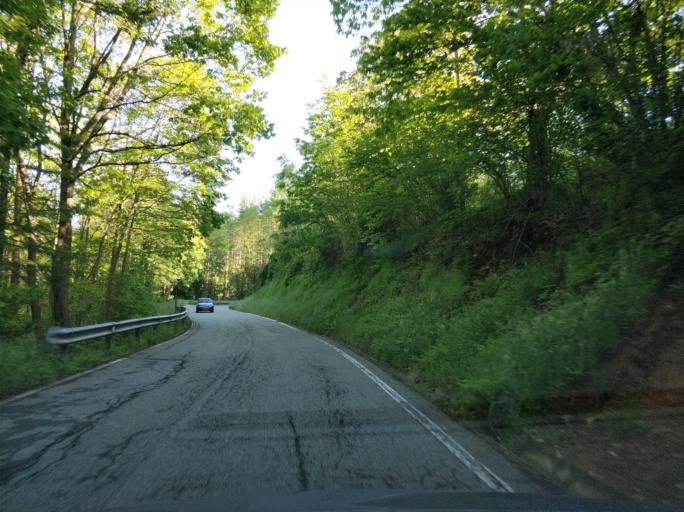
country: IT
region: Piedmont
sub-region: Provincia di Torino
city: Coassolo
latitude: 45.2926
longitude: 7.4696
